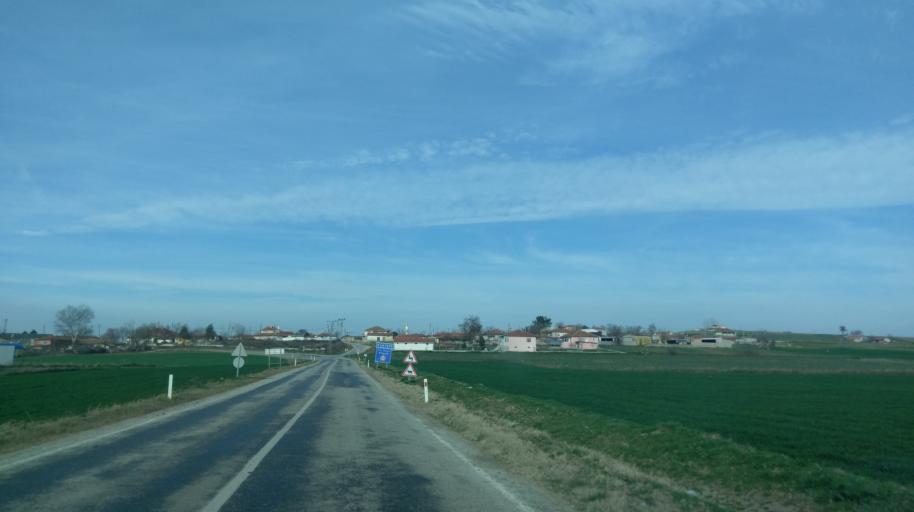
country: TR
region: Kirklareli
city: Pehlivankoy
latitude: 41.3717
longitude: 26.9659
